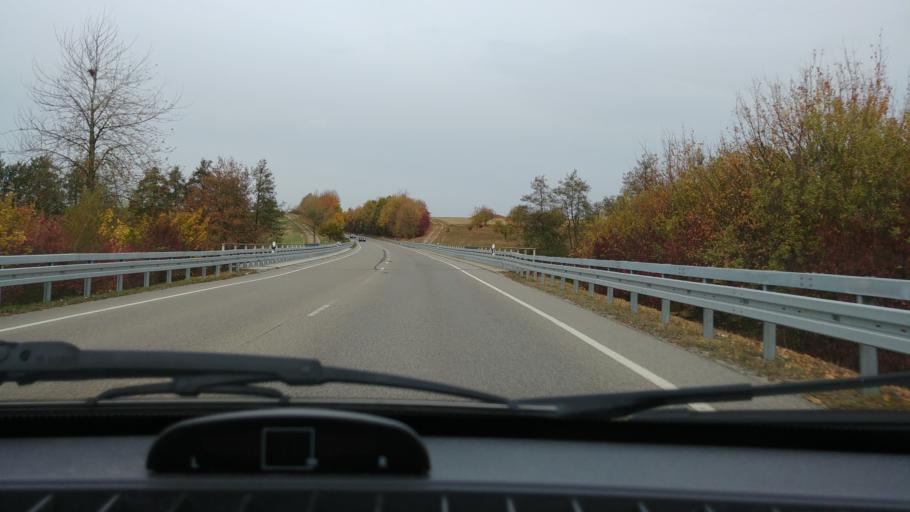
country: DE
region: Baden-Wuerttemberg
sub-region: Regierungsbezirk Stuttgart
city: Satteldorf
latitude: 49.1599
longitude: 10.0762
